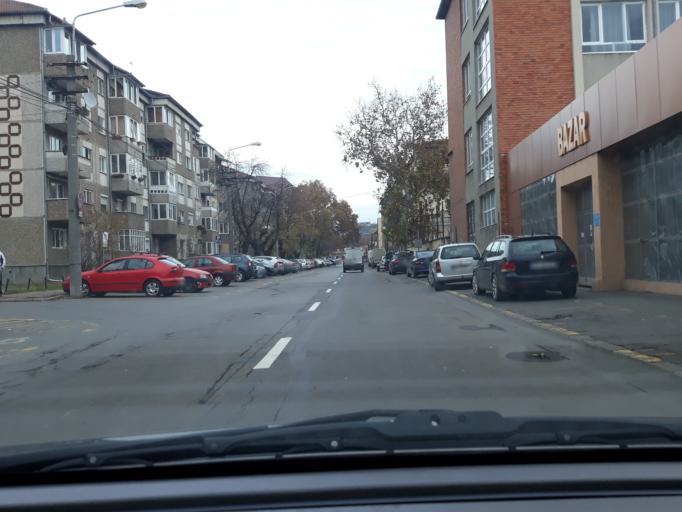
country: RO
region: Bihor
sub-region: Comuna Biharea
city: Oradea
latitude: 47.0655
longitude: 21.9247
